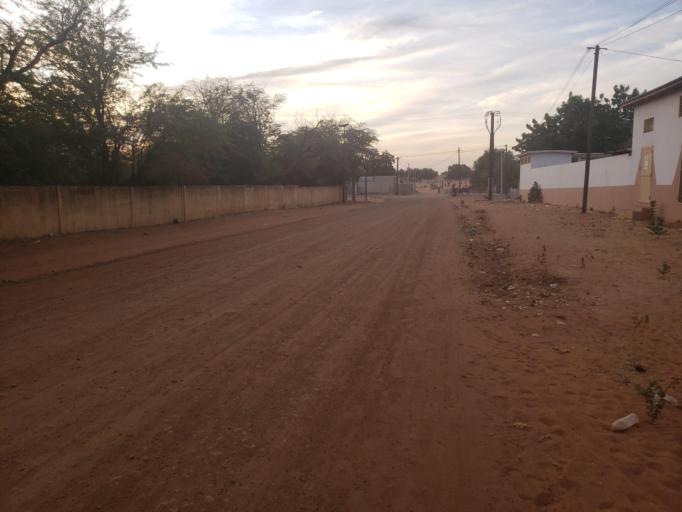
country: SN
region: Louga
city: Ndibene Dahra
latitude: 15.4003
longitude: -15.1122
